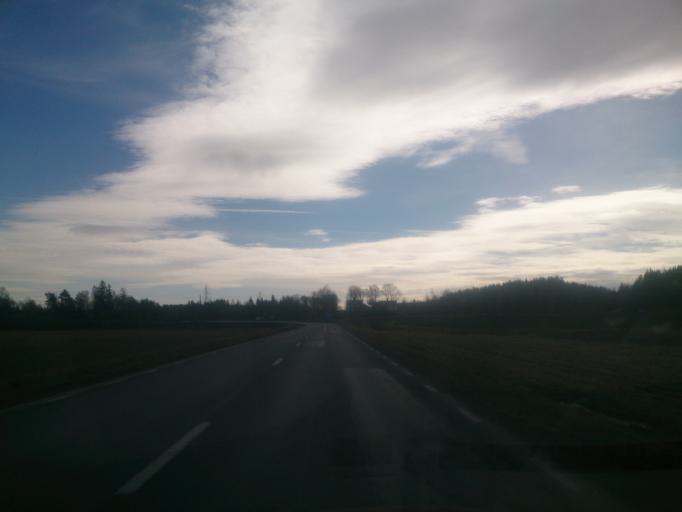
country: SE
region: OEstergoetland
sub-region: Norrkopings Kommun
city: Skarblacka
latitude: 58.5972
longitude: 15.8359
